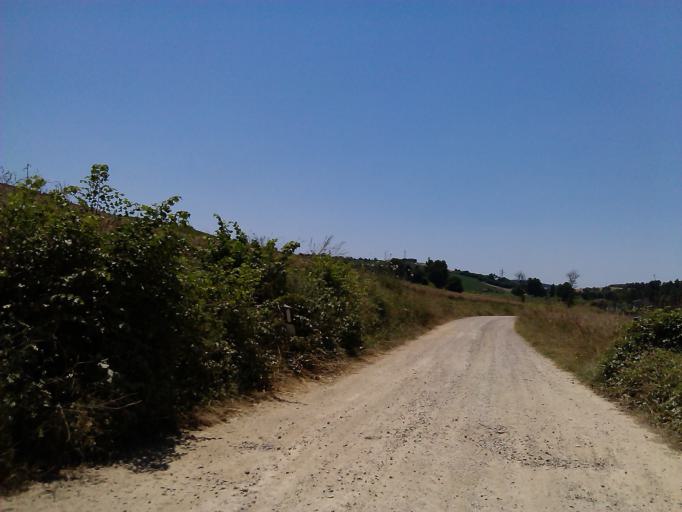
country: IT
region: Umbria
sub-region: Provincia di Terni
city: Fabro Scalo
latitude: 42.8503
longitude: 12.0408
